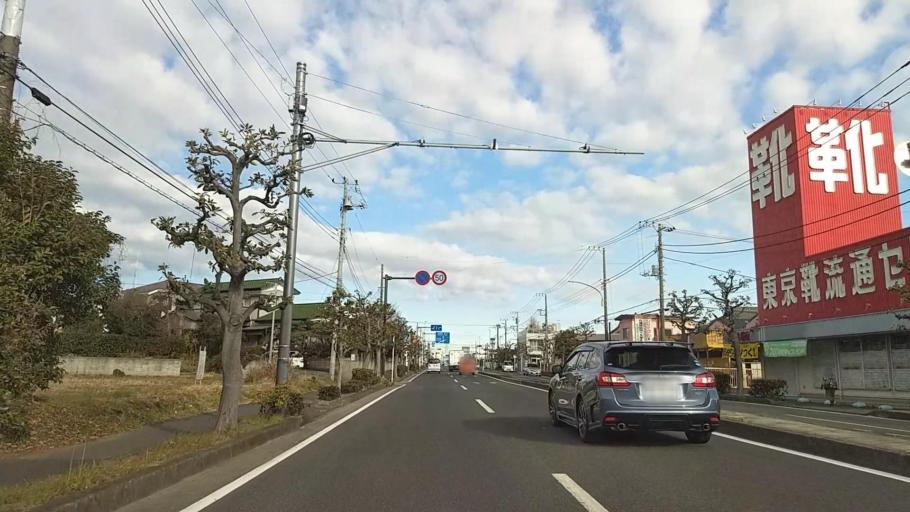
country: JP
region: Kanagawa
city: Hiratsuka
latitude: 35.3465
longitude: 139.3563
